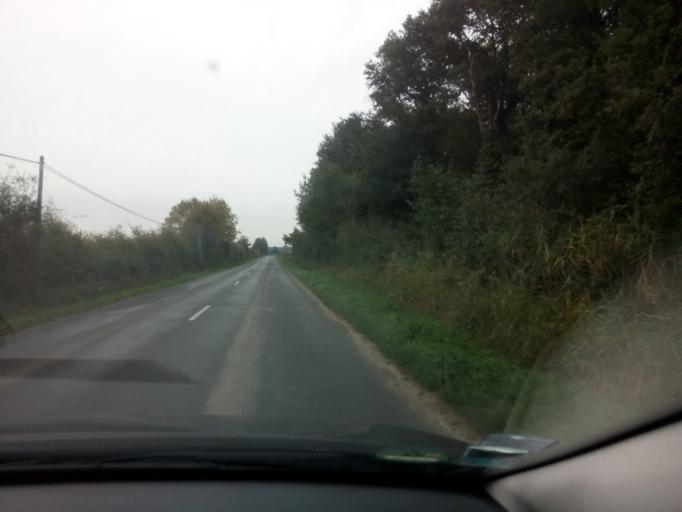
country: FR
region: Pays de la Loire
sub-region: Departement de Maine-et-Loire
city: Tierce
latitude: 47.6163
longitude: -0.4451
